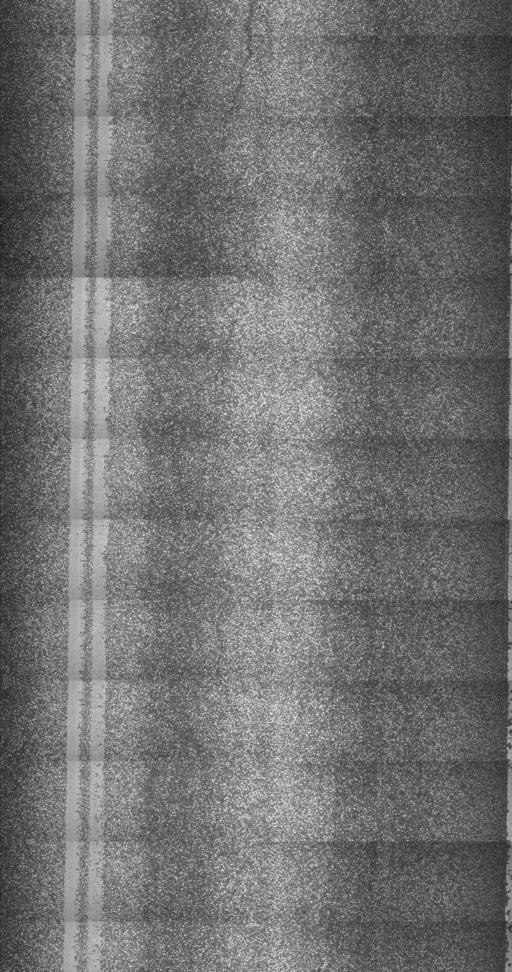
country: US
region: Vermont
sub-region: Washington County
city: Montpelier
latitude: 44.3402
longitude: -72.5670
